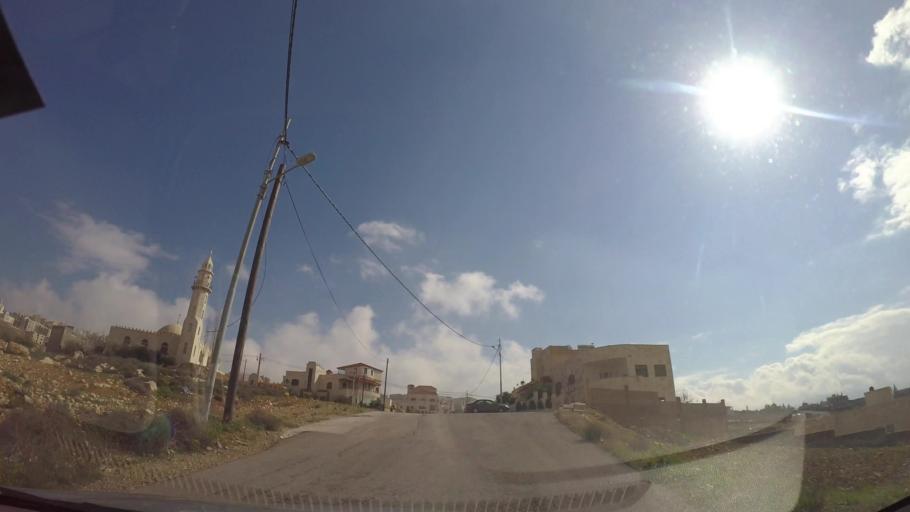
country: JO
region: Amman
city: Al Jubayhah
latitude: 32.0717
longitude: 35.8705
